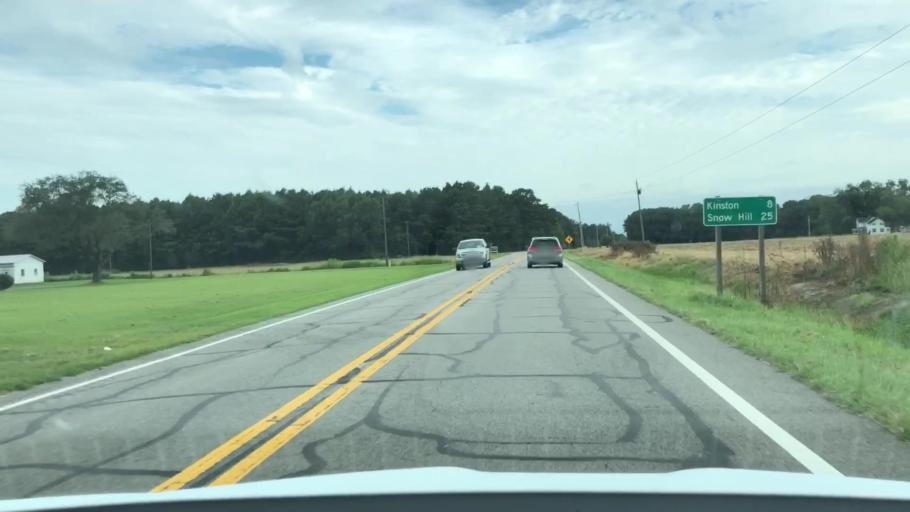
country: US
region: North Carolina
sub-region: Lenoir County
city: Kinston
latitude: 35.1608
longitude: -77.5553
